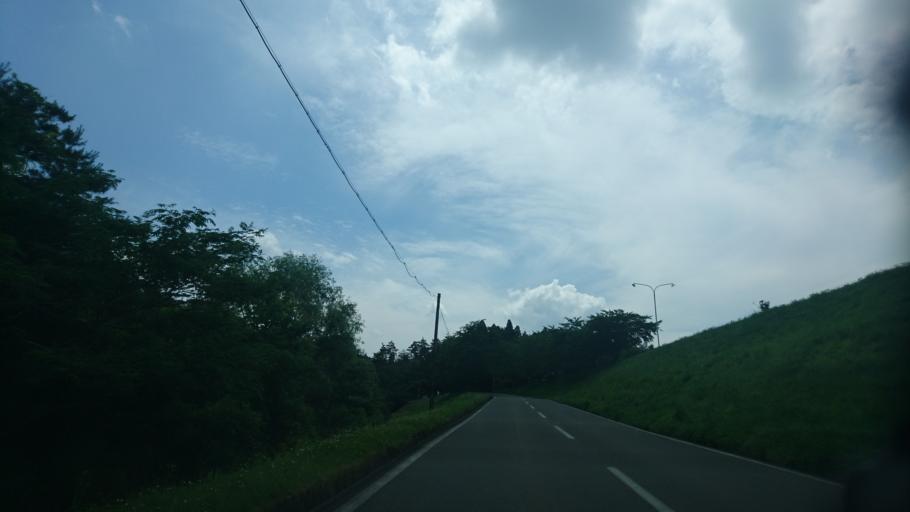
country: JP
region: Iwate
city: Ichinoseki
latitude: 38.9067
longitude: 141.3546
